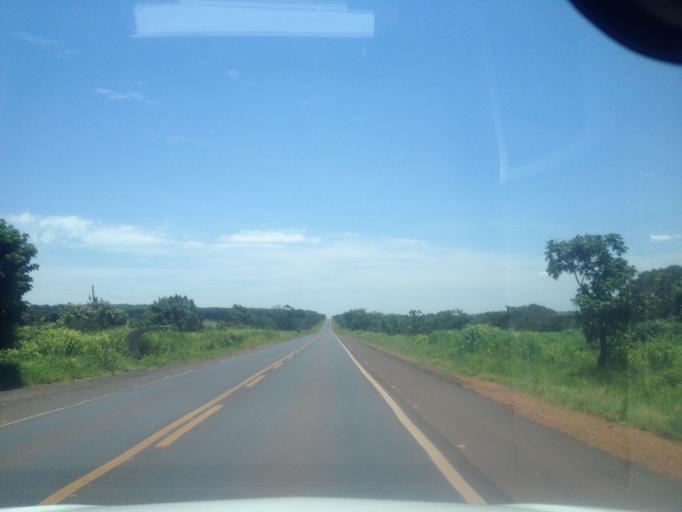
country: BR
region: Minas Gerais
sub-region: Monte Alegre De Minas
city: Monte Alegre de Minas
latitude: -18.8797
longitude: -49.1175
